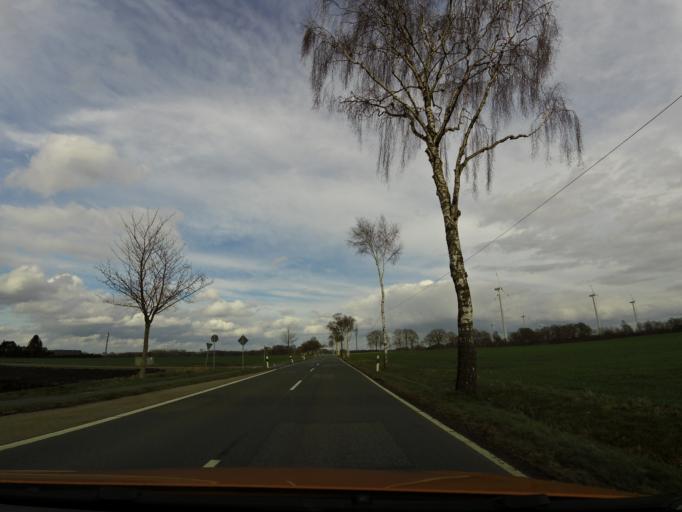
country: DE
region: Lower Saxony
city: Prinzhofte
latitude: 52.9310
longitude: 8.5289
